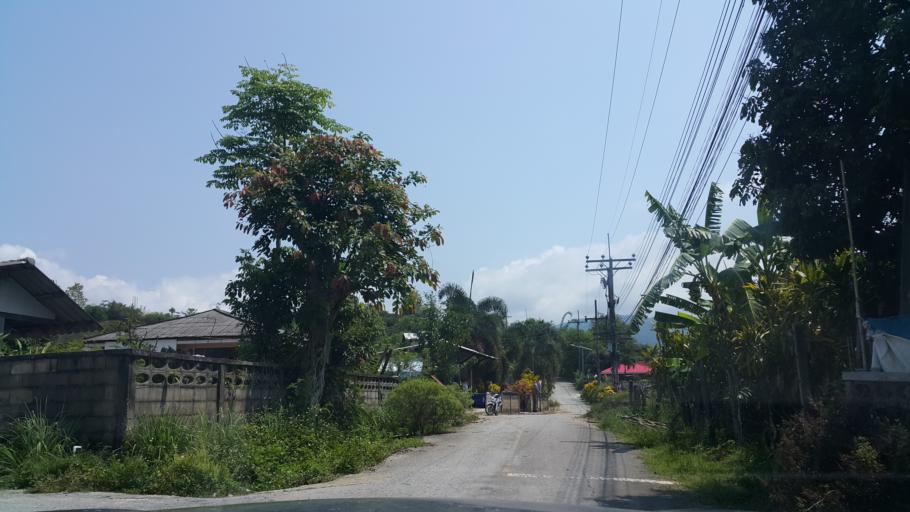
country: TH
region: Chiang Rai
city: Chiang Rai
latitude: 19.9751
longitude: 99.7626
